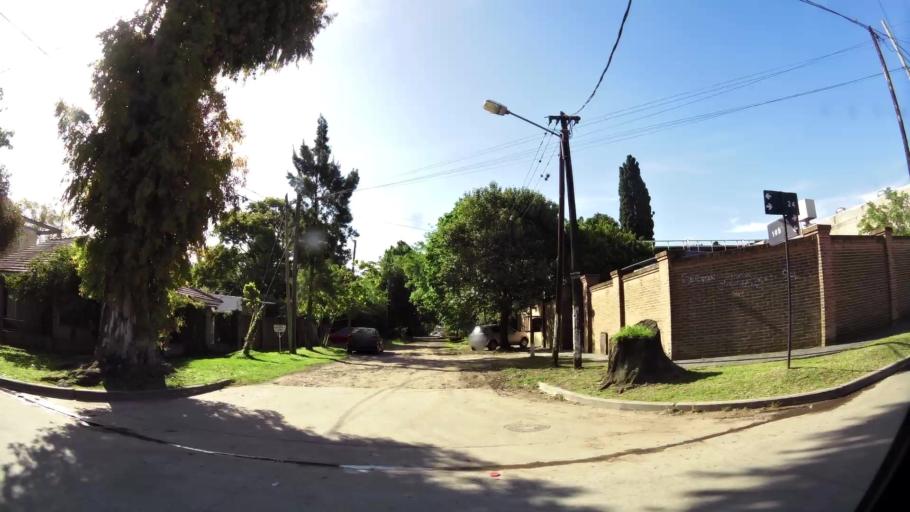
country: AR
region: Buenos Aires
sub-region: Partido de Quilmes
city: Quilmes
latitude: -34.7942
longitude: -58.2446
